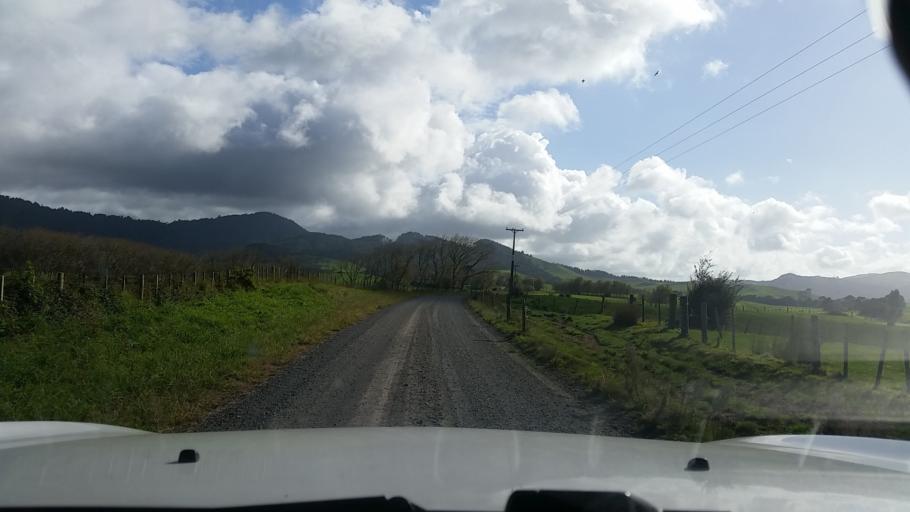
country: NZ
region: Waikato
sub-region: Hauraki District
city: Ngatea
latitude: -37.5093
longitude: 175.4077
